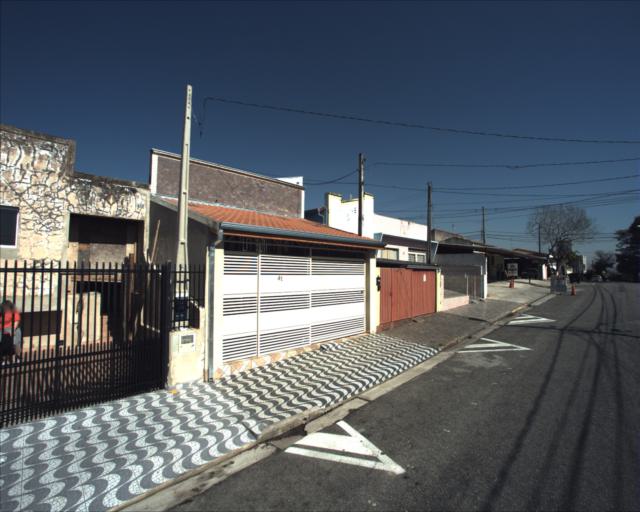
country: BR
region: Sao Paulo
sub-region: Sorocaba
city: Sorocaba
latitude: -23.5077
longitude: -47.4367
